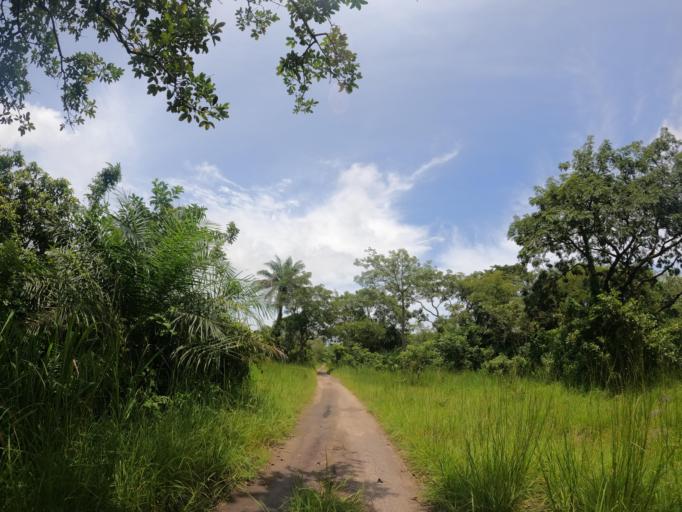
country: SL
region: Northern Province
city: Binkolo
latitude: 9.1428
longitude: -12.2419
